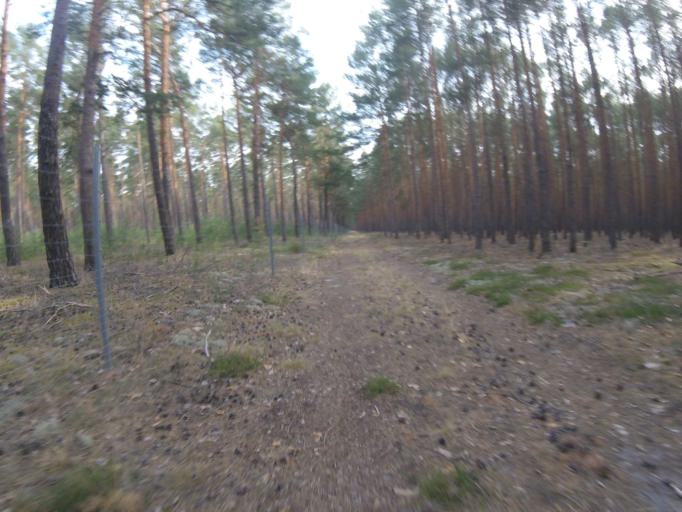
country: DE
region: Brandenburg
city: Bestensee
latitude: 52.2378
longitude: 13.7562
